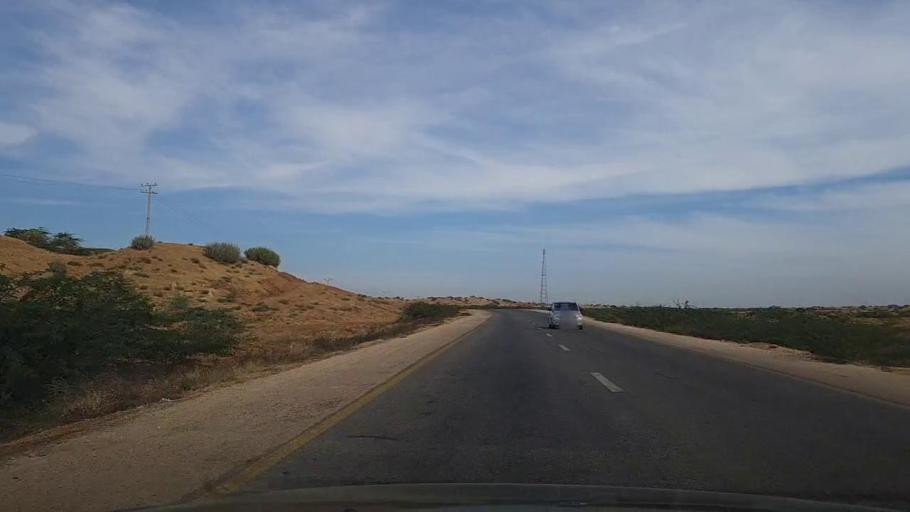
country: PK
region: Sindh
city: Thatta
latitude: 24.8592
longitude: 68.0235
